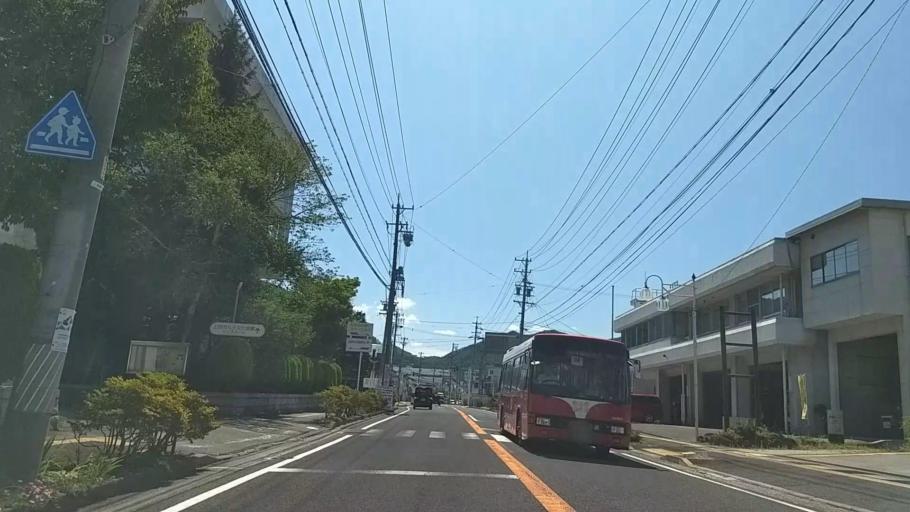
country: JP
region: Nagano
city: Kamimaruko
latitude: 36.3242
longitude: 138.2698
